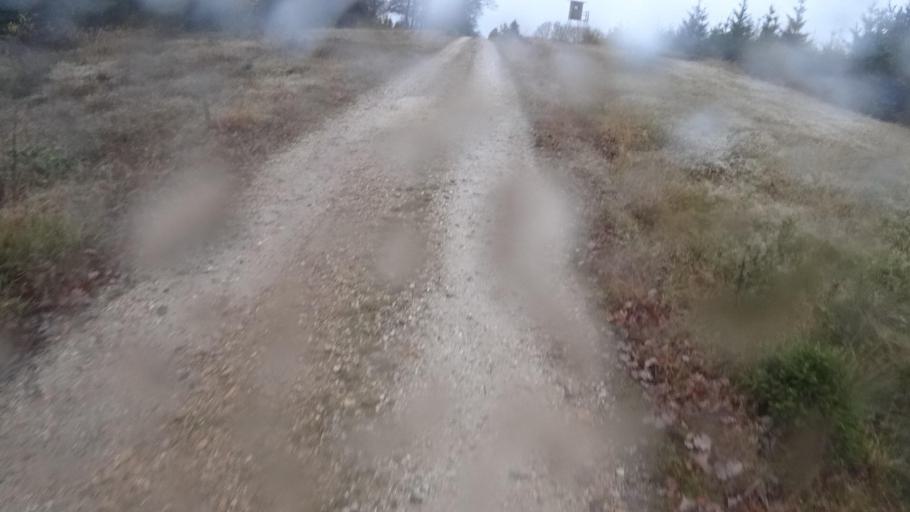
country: DE
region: Rheinland-Pfalz
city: Birkheim
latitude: 50.1009
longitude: 7.6100
